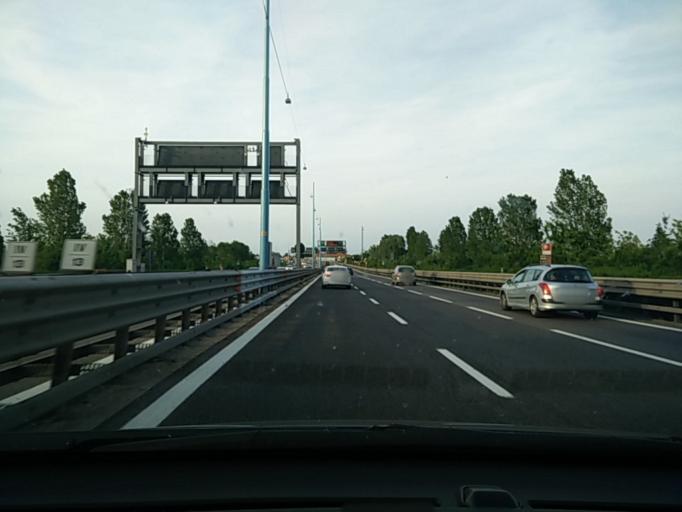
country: IT
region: Veneto
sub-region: Provincia di Venezia
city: Mestre
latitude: 45.4951
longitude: 12.2269
